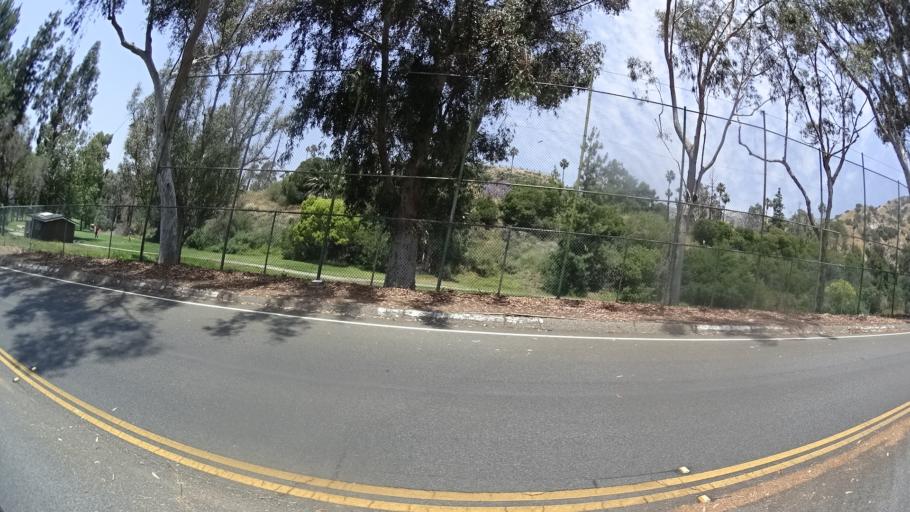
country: US
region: California
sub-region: Los Angeles County
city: Burbank
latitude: 34.2024
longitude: -118.3009
